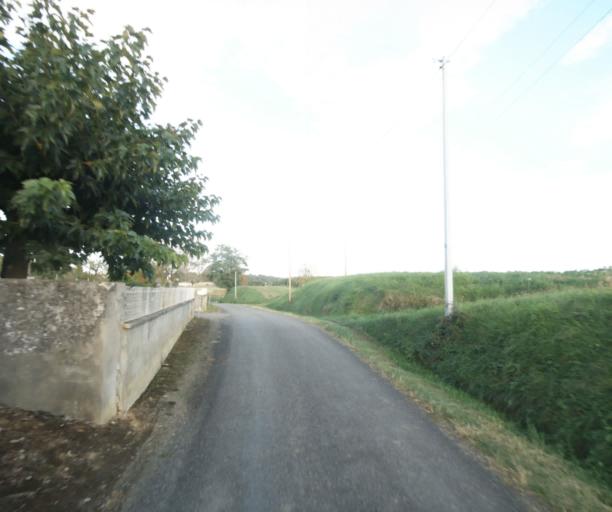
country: FR
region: Midi-Pyrenees
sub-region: Departement du Gers
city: Le Houga
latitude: 43.8420
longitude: -0.1209
